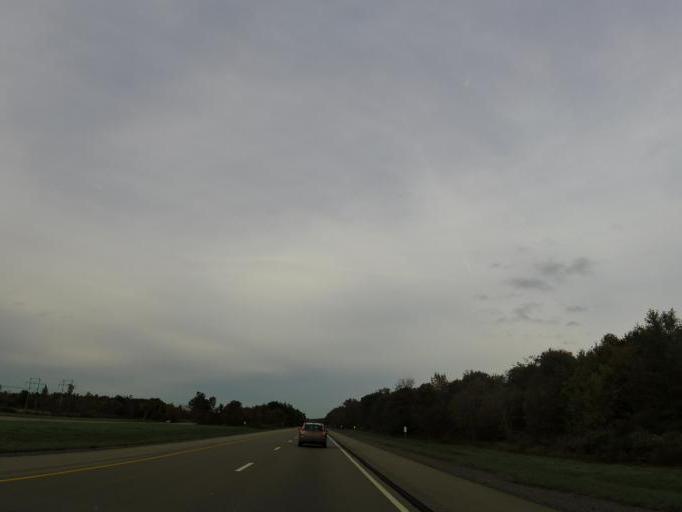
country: US
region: New York
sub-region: Erie County
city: Angola
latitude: 42.6000
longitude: -79.0354
